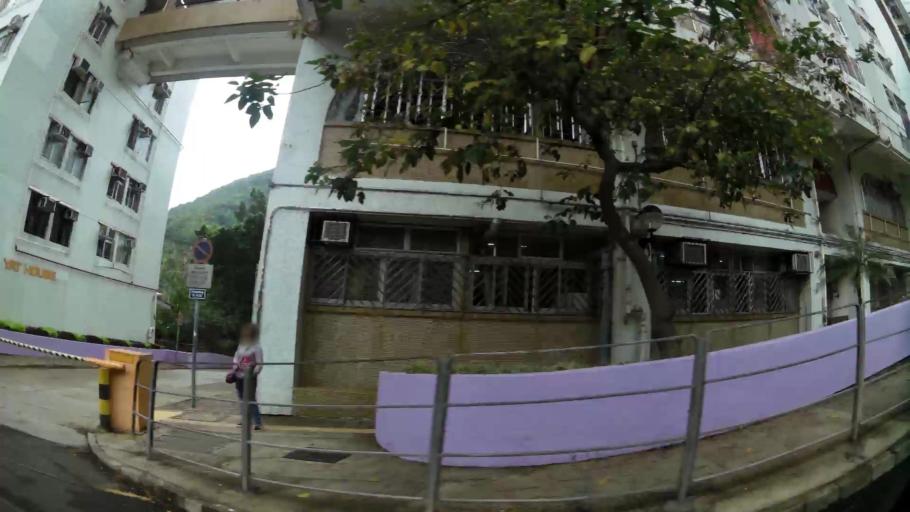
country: HK
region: Central and Western
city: Central
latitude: 22.2408
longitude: 114.1574
